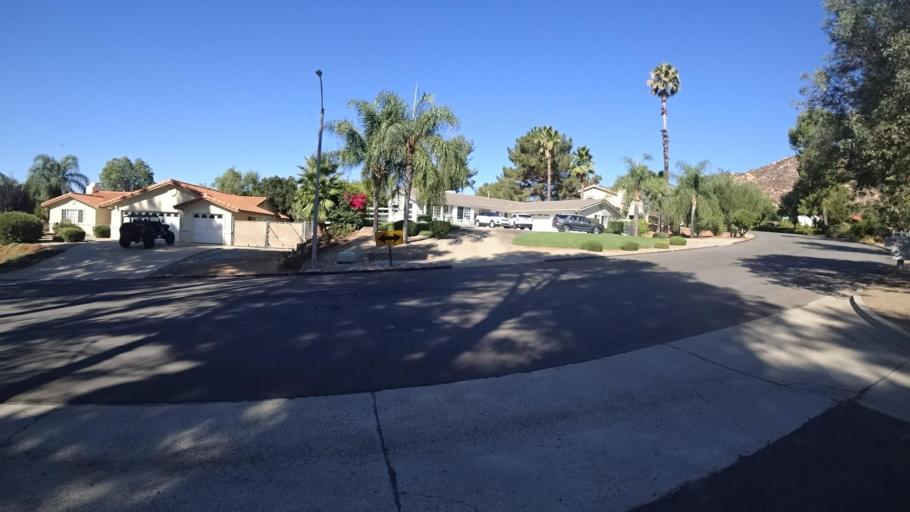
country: US
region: California
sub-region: San Diego County
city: San Diego Country Estates
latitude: 33.0014
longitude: -116.7590
